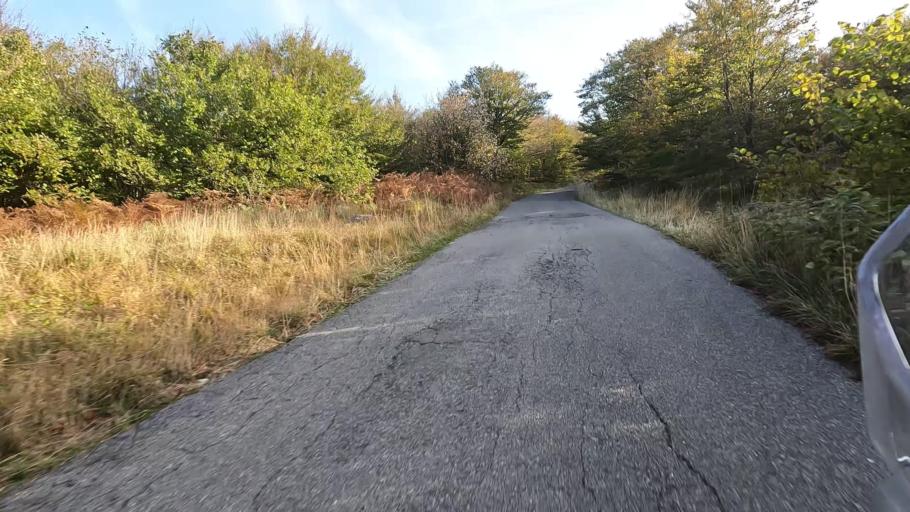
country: IT
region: Liguria
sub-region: Provincia di Genova
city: Sciarborasca
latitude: 44.4333
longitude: 8.5866
